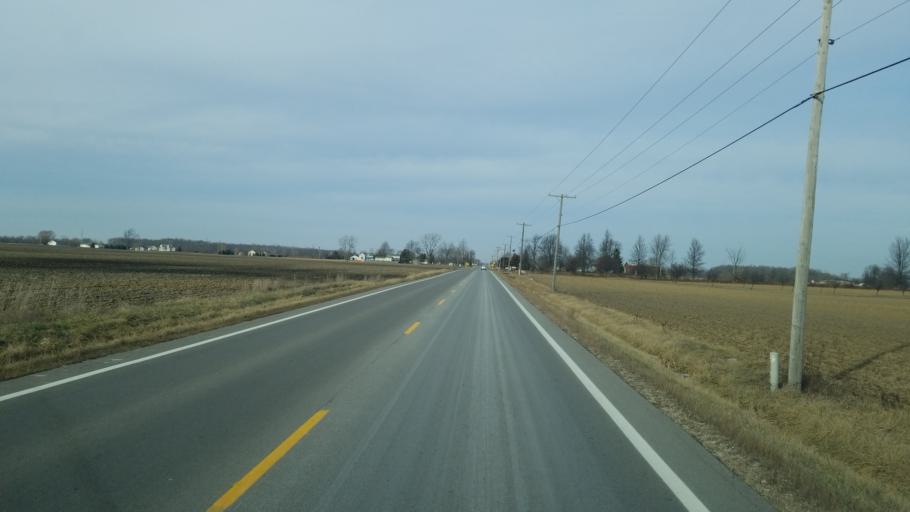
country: US
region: Ohio
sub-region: Union County
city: Marysville
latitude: 40.3394
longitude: -83.3941
